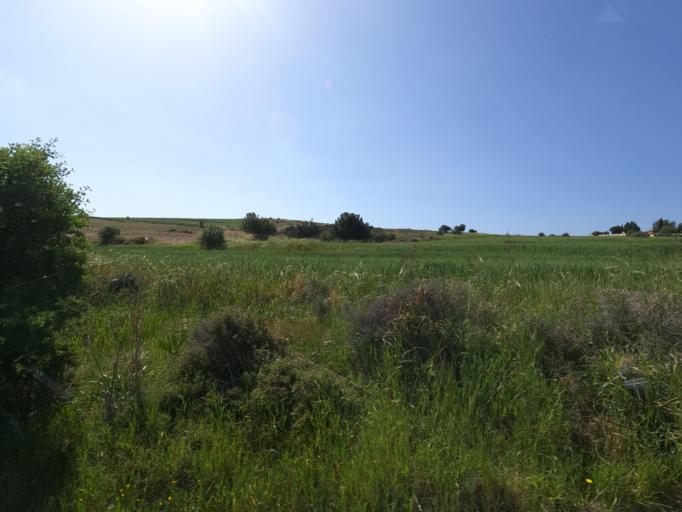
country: CY
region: Lefkosia
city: Astromeritis
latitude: 35.0875
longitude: 33.0212
